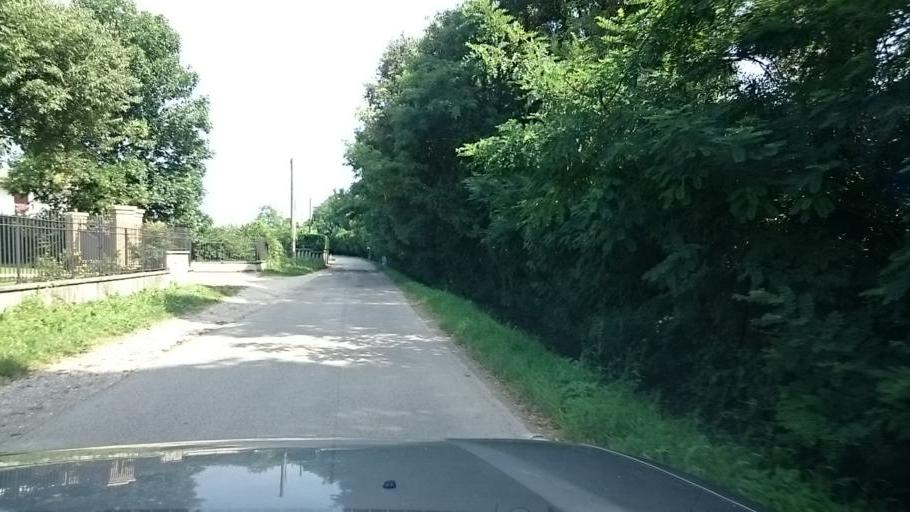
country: IT
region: Veneto
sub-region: Provincia di Vicenza
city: Rossano Veneto
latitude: 45.6888
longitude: 11.8188
